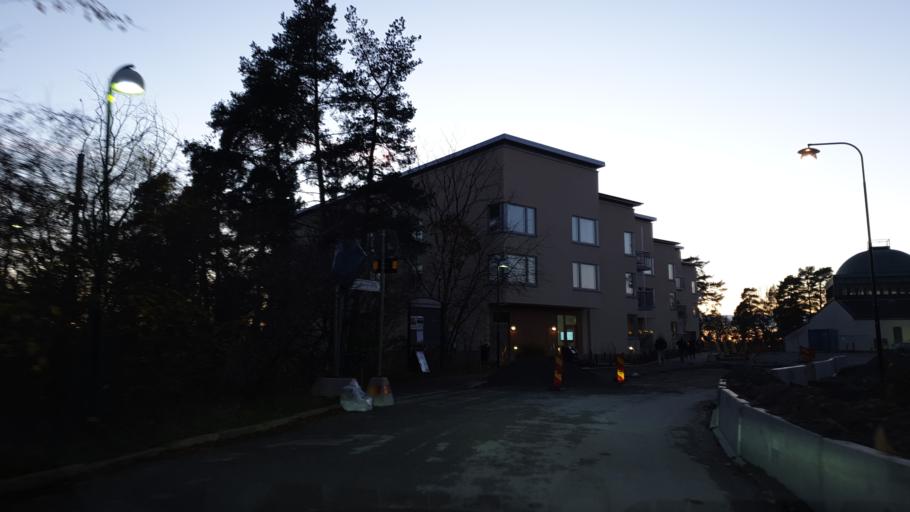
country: SE
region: Stockholm
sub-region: Stockholms Kommun
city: Bromma
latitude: 59.3287
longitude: 17.9181
